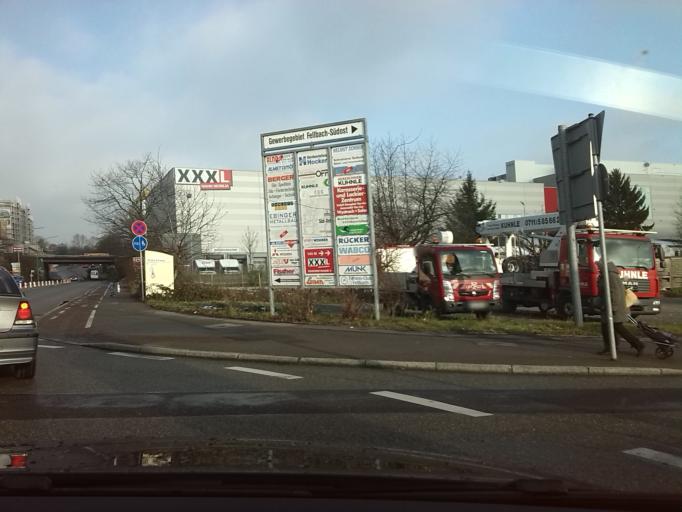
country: DE
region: Baden-Wuerttemberg
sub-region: Regierungsbezirk Stuttgart
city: Fellbach
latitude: 48.8143
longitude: 9.2843
